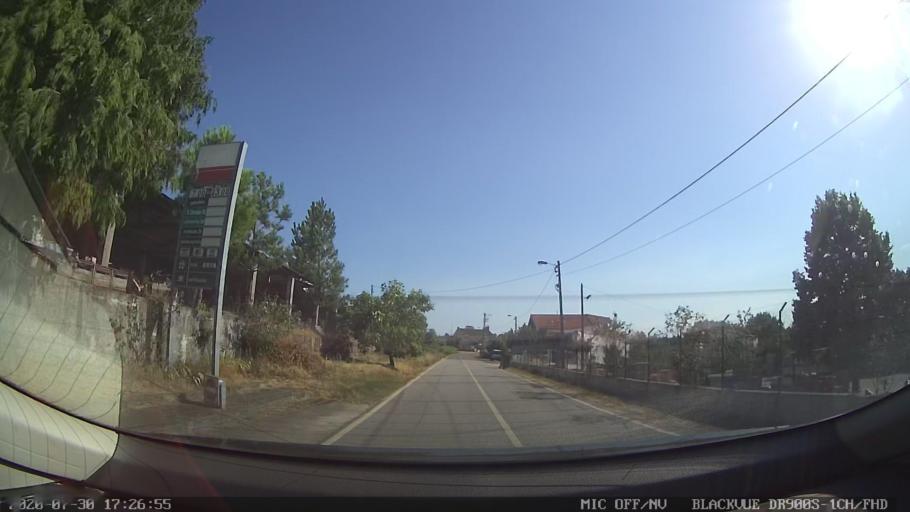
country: PT
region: Vila Real
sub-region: Murca
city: Murca
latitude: 41.3198
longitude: -7.4621
